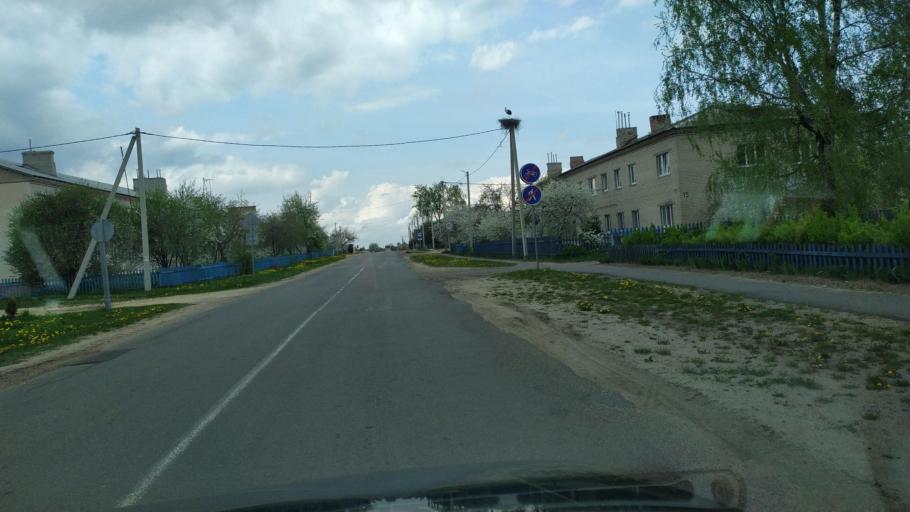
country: BY
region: Brest
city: Pruzhany
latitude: 52.5654
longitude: 24.4196
